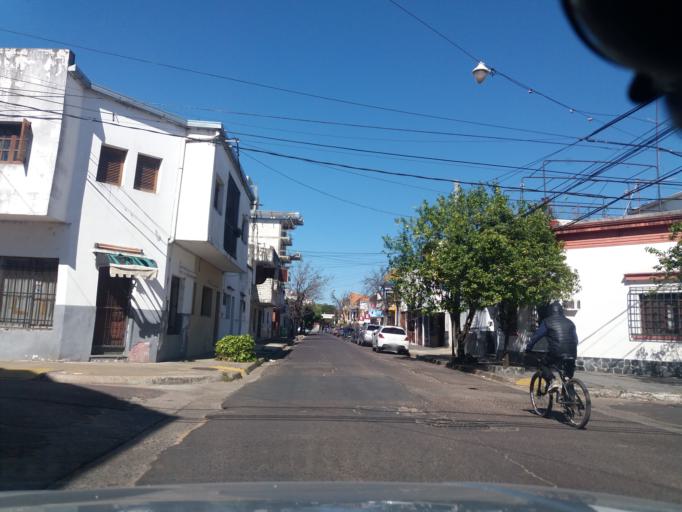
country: AR
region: Corrientes
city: Corrientes
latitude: -27.4728
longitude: -58.8420
